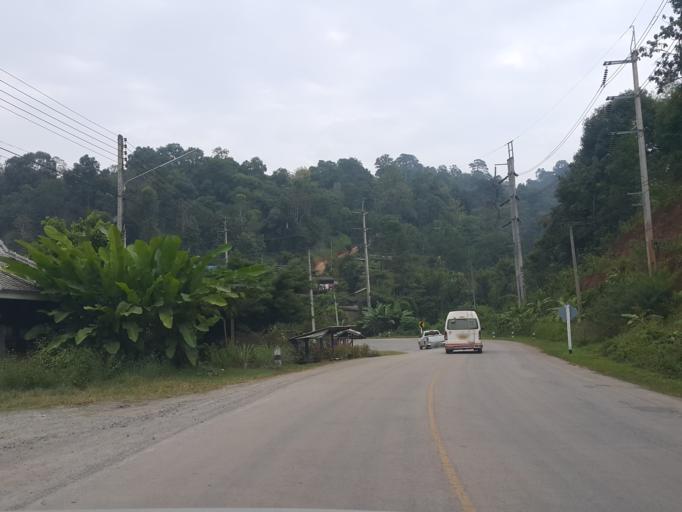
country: TH
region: Chiang Mai
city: Mae Taeng
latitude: 19.1162
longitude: 98.7311
